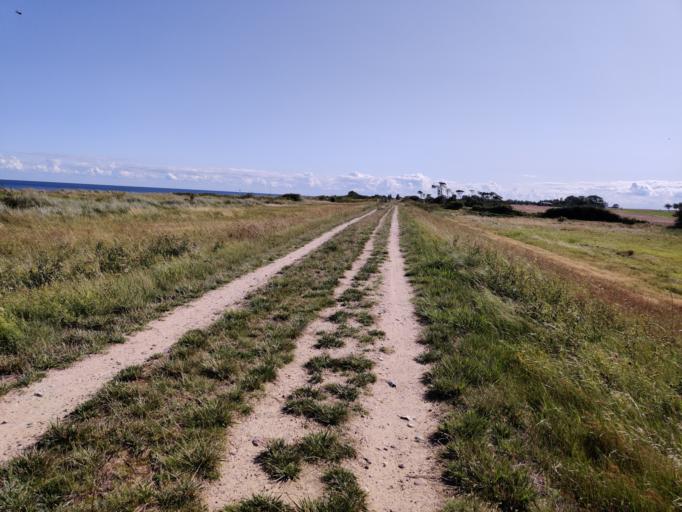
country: DK
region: Zealand
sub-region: Guldborgsund Kommune
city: Nykobing Falster
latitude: 54.5806
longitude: 11.9719
